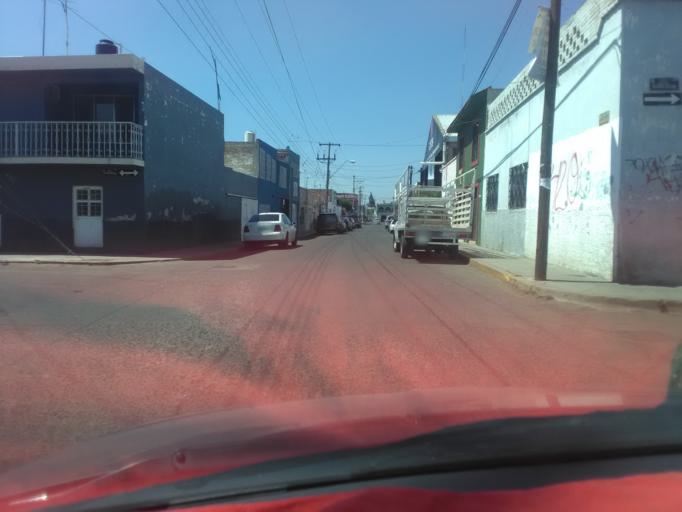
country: MX
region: Durango
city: Victoria de Durango
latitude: 24.0211
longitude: -104.6602
